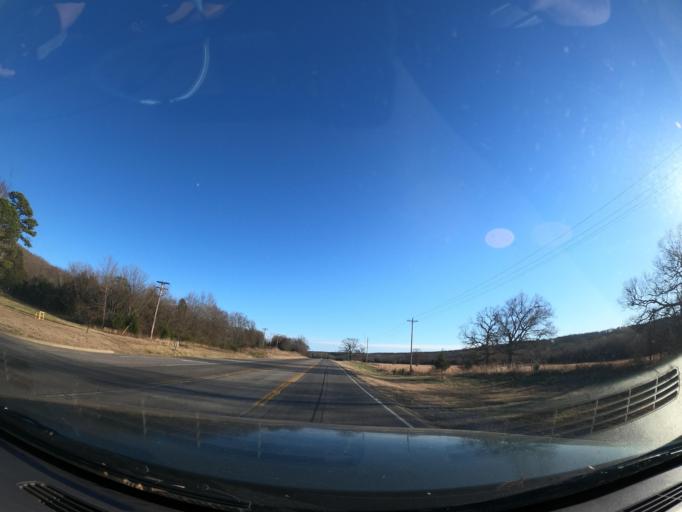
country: US
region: Oklahoma
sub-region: Latimer County
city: Wilburton
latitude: 34.9312
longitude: -95.3383
